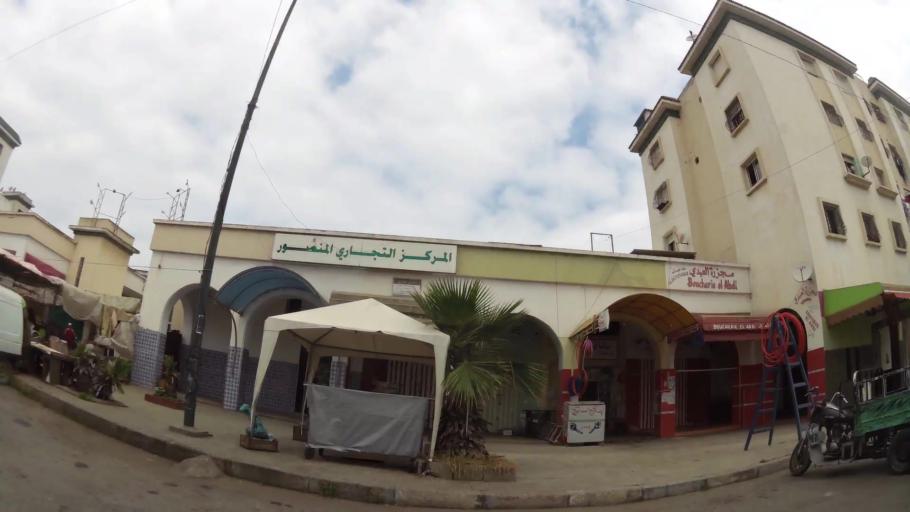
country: MA
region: Rabat-Sale-Zemmour-Zaer
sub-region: Rabat
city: Rabat
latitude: 33.9950
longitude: -6.8772
